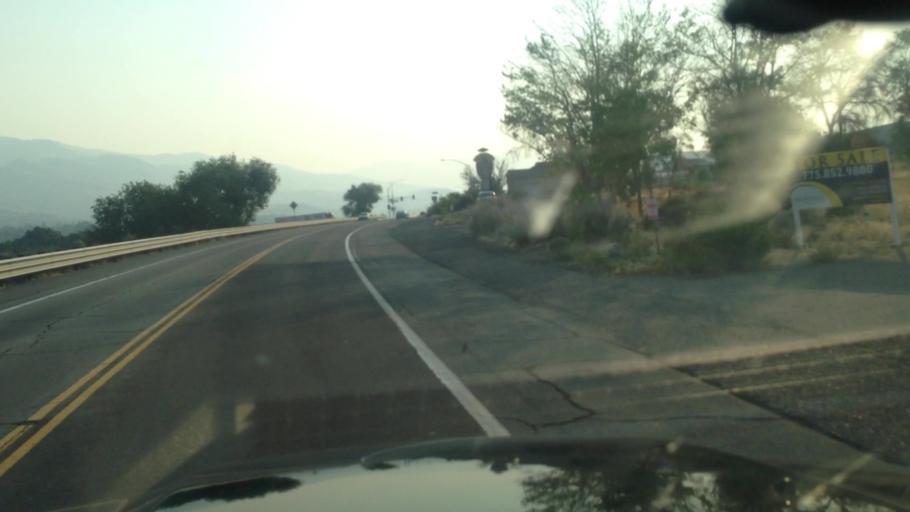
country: US
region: Nevada
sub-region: Washoe County
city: Reno
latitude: 39.5133
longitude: -119.8558
